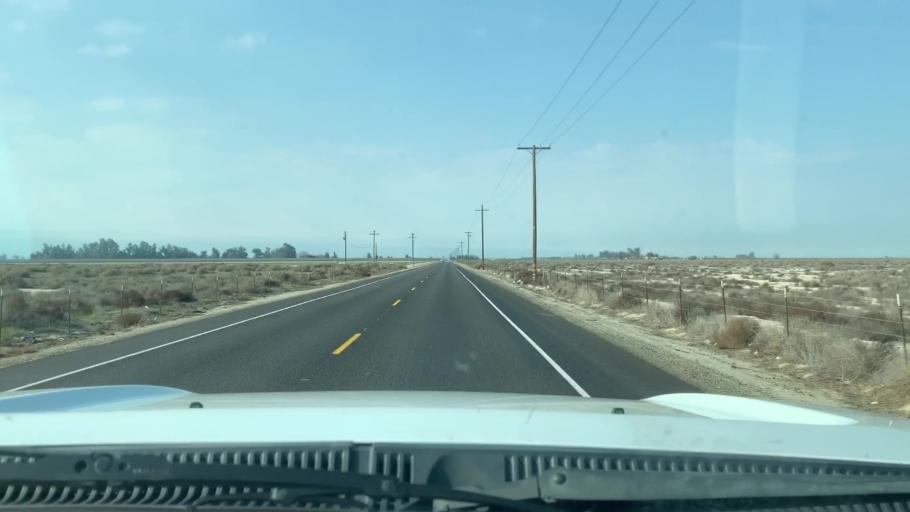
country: US
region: California
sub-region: Kern County
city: Buttonwillow
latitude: 35.4422
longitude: -119.3916
